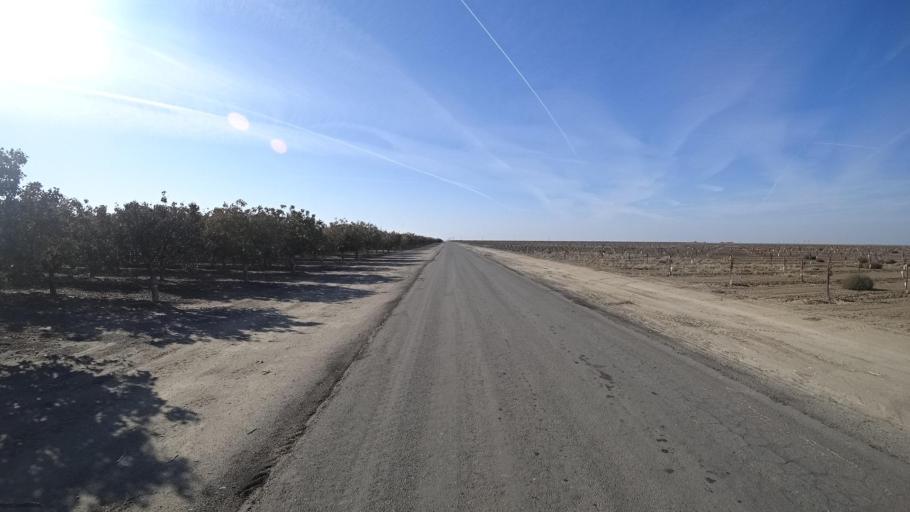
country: US
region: California
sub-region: Kern County
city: Wasco
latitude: 35.6887
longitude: -119.4121
